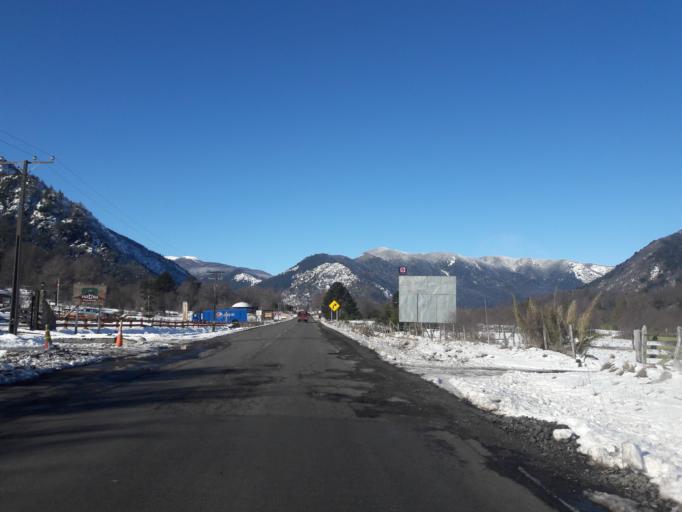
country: CL
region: Araucania
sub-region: Provincia de Cautin
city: Vilcun
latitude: -38.4720
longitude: -71.5667
